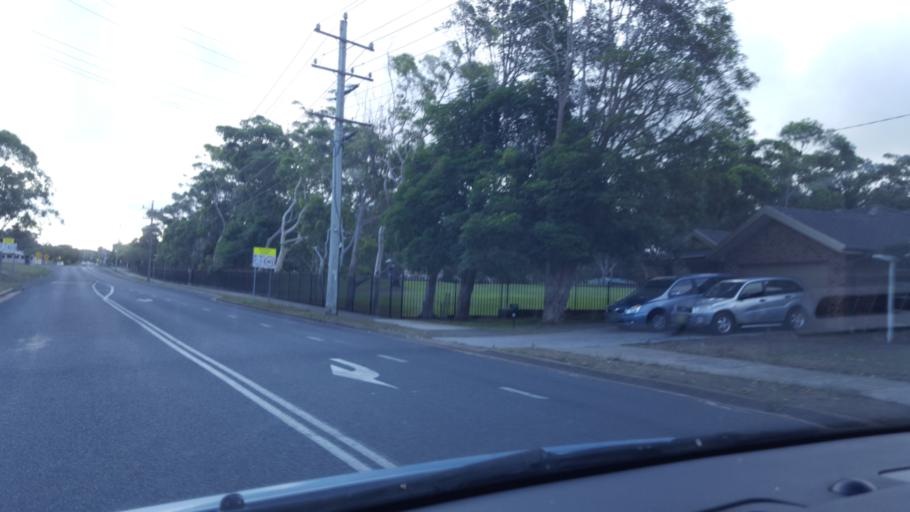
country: AU
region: New South Wales
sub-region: Port Stephens Shire
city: Anna Bay
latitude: -32.7765
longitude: 152.0925
